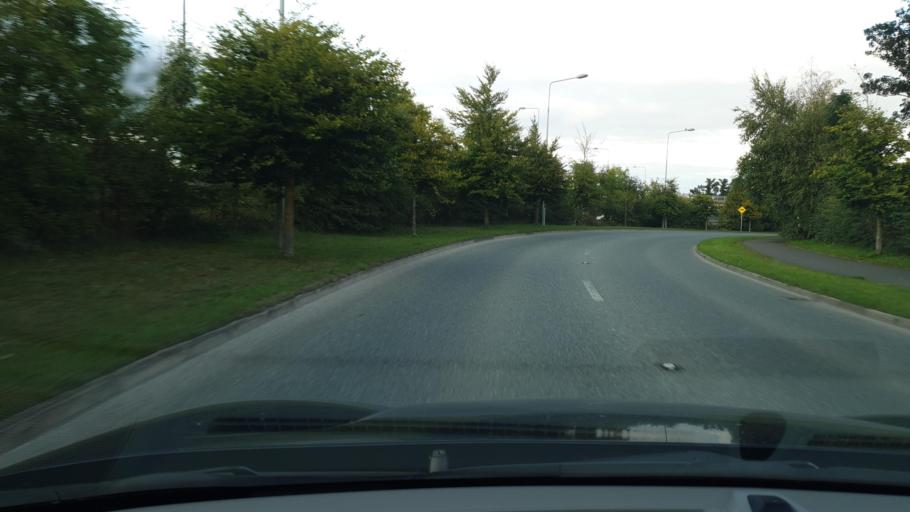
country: IE
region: Leinster
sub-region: Kildare
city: Johnstown
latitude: 53.2350
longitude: -6.6278
